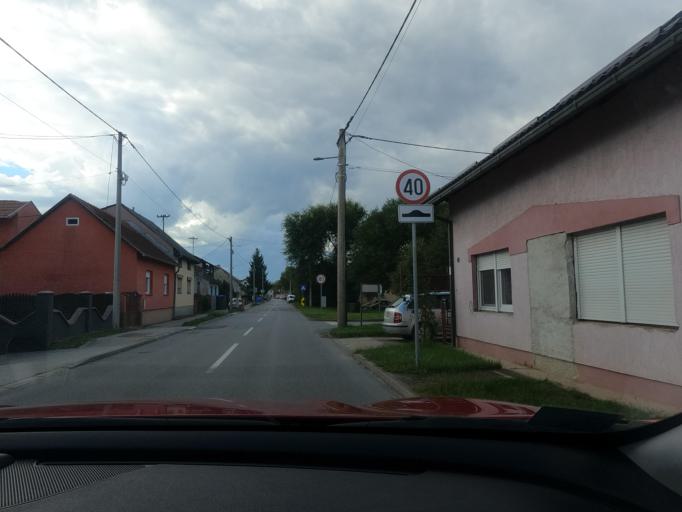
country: HR
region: Sisacko-Moslavacka
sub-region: Grad Sisak
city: Sisak
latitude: 45.4852
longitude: 16.3851
